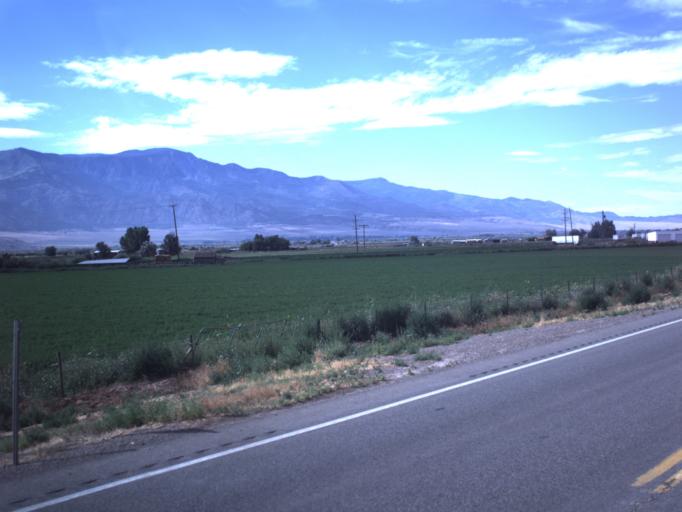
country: US
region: Utah
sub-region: Sevier County
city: Richfield
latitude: 38.7792
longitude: -112.0624
